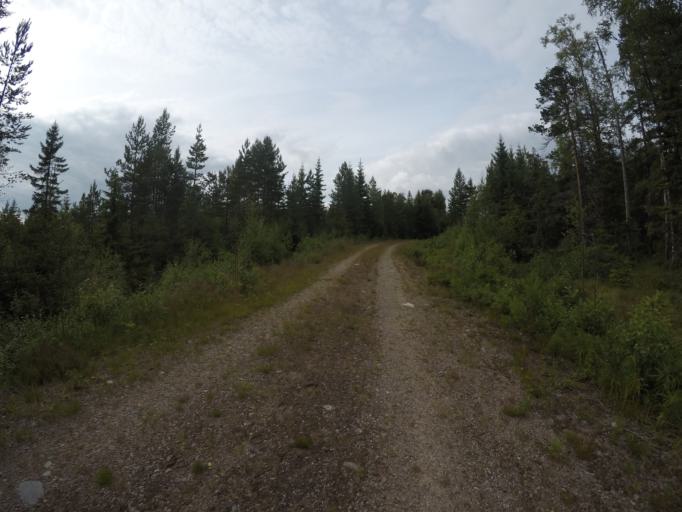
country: SE
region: Vaermland
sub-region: Filipstads Kommun
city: Lesjofors
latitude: 60.2104
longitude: 14.2613
